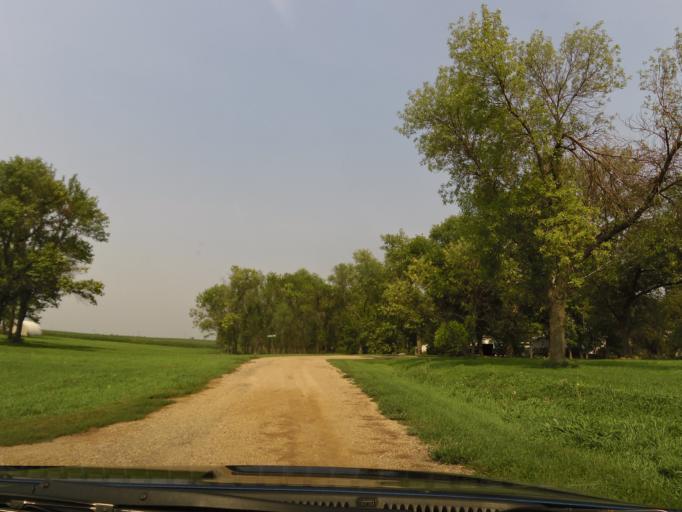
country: US
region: South Dakota
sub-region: Roberts County
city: Sisseton
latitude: 45.8563
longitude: -97.1072
